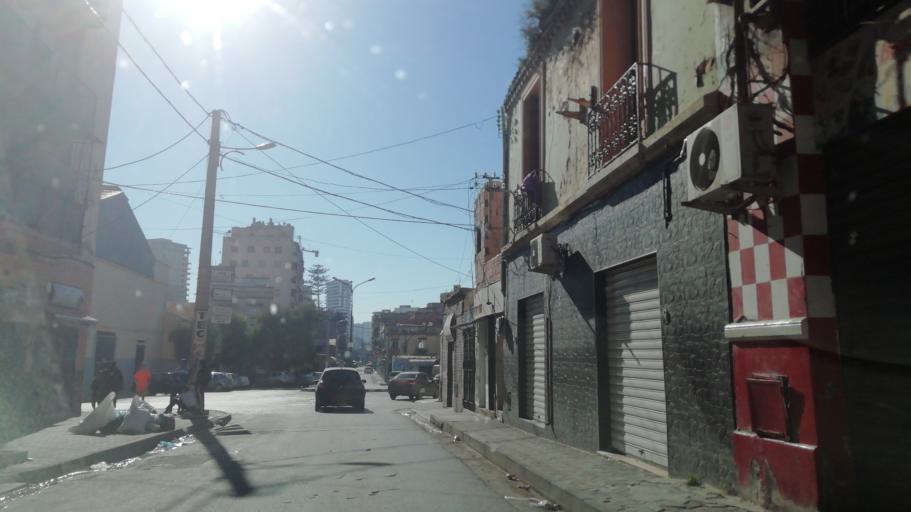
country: DZ
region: Oran
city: Oran
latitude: 35.7086
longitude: -0.6190
